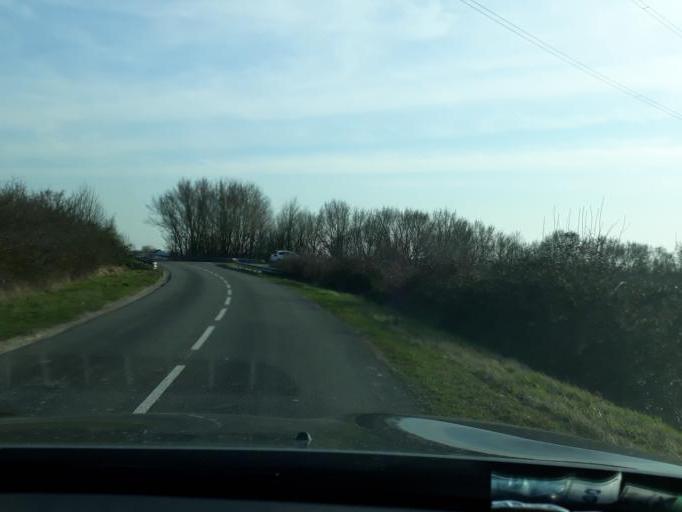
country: FR
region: Centre
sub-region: Departement du Loiret
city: Meung-sur-Loire
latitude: 47.8482
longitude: 1.6820
